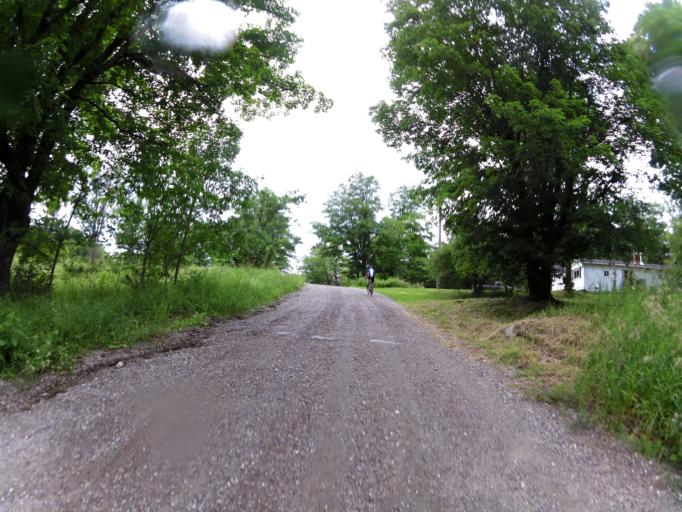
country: CA
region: Ontario
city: Renfrew
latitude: 45.0653
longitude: -76.7574
